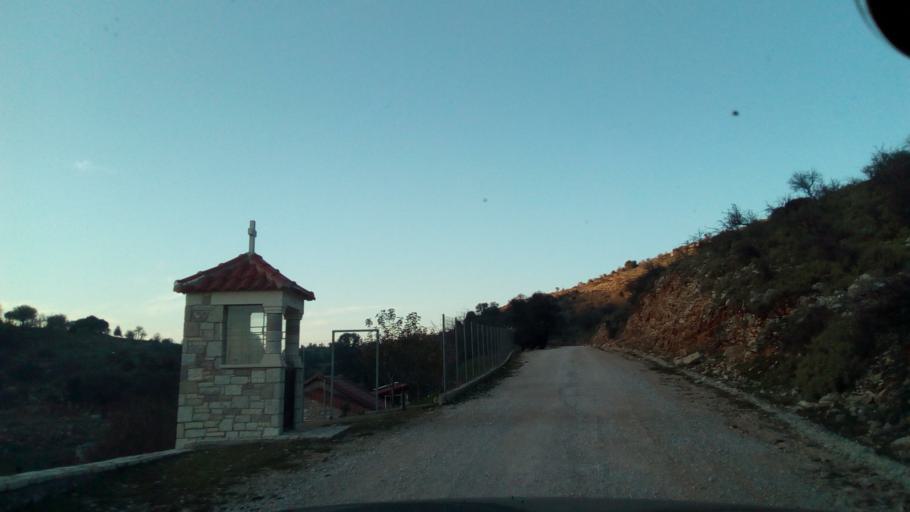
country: GR
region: West Greece
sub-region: Nomos Aitolias kai Akarnanias
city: Nafpaktos
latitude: 38.4583
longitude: 21.8387
